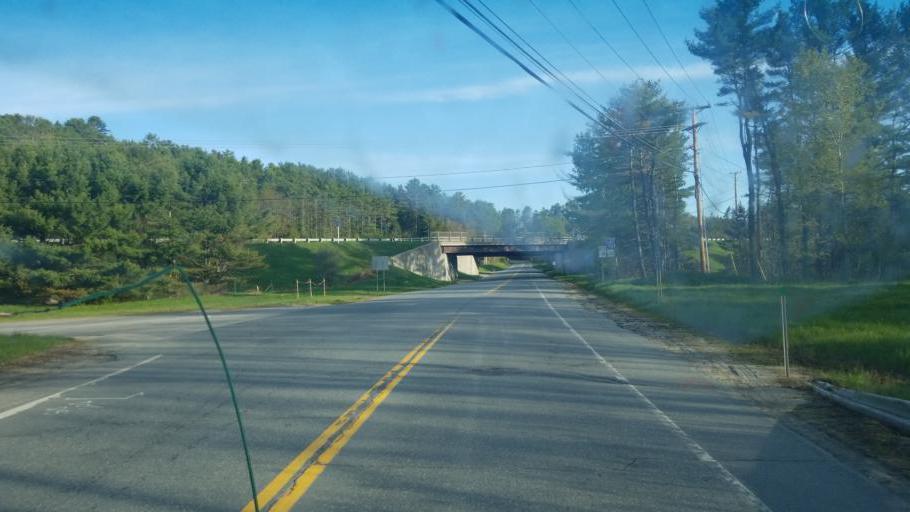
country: US
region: New Hampshire
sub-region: Grafton County
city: Littleton
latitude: 44.3160
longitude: -71.7966
